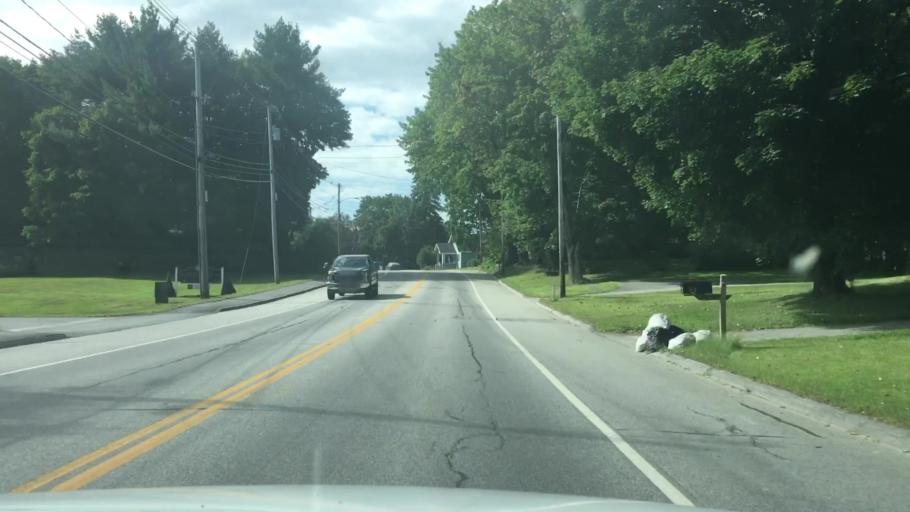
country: US
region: Maine
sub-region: Androscoggin County
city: Auburn
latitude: 44.1136
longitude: -70.2328
